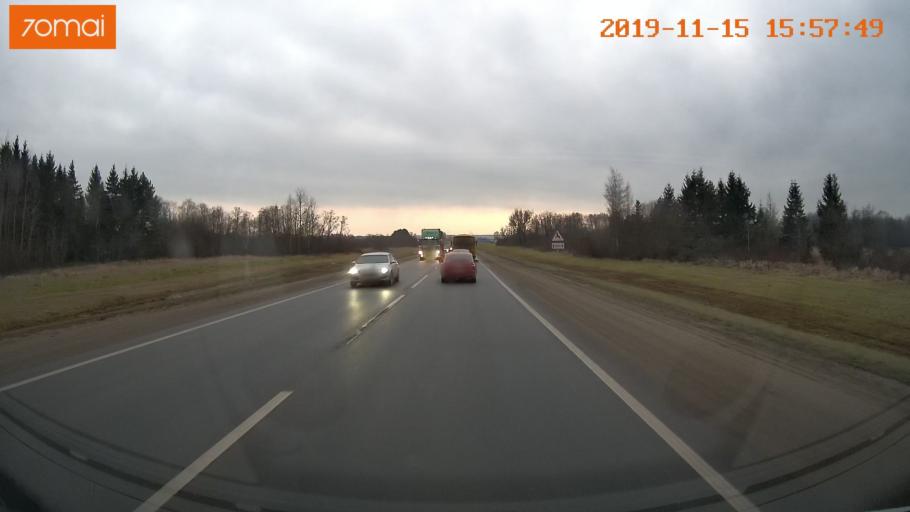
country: RU
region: Jaroslavl
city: Yaroslavl
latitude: 57.8264
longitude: 39.9602
